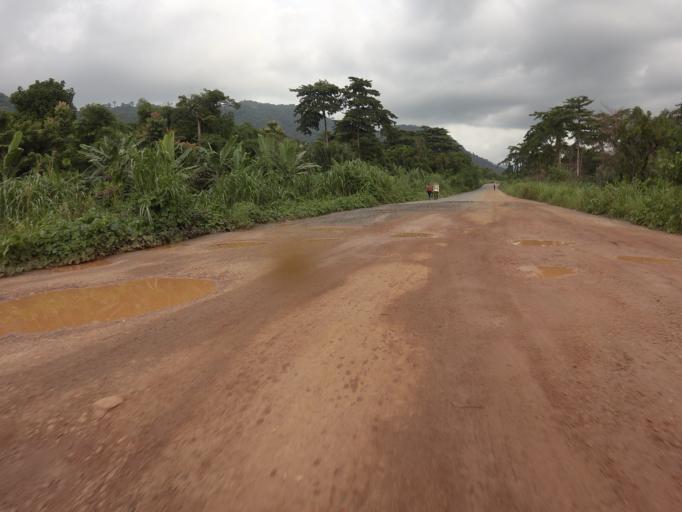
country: GH
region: Volta
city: Kpandu
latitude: 6.8101
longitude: 0.3749
